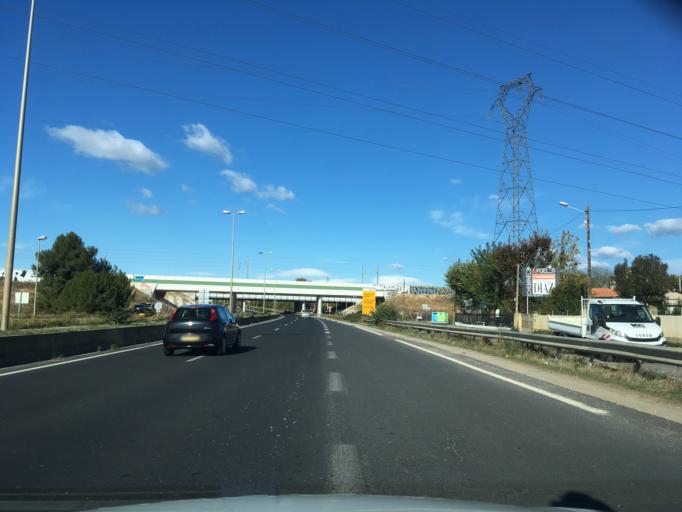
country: FR
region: Languedoc-Roussillon
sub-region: Departement de l'Herault
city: Lattes
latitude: 43.5817
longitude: 3.8982
